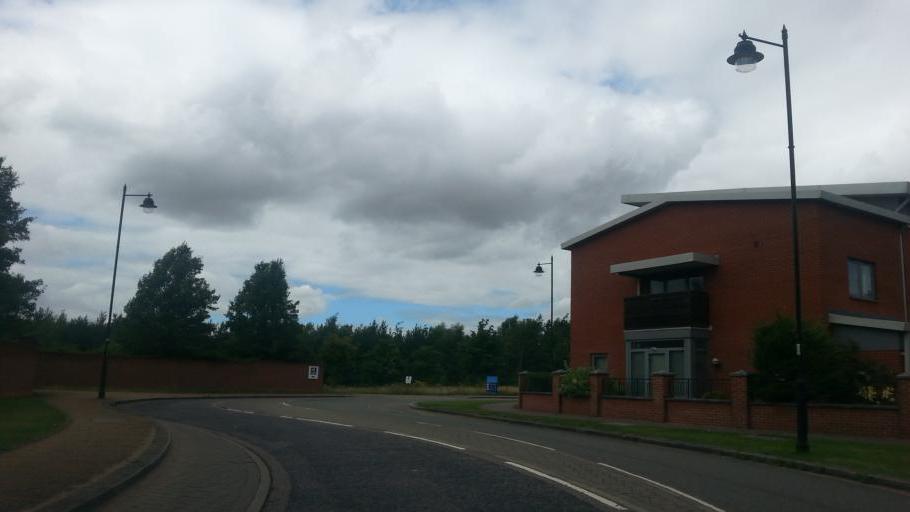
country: GB
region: England
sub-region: Cambridgeshire
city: Papworth Everard
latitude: 52.2200
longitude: -0.0709
